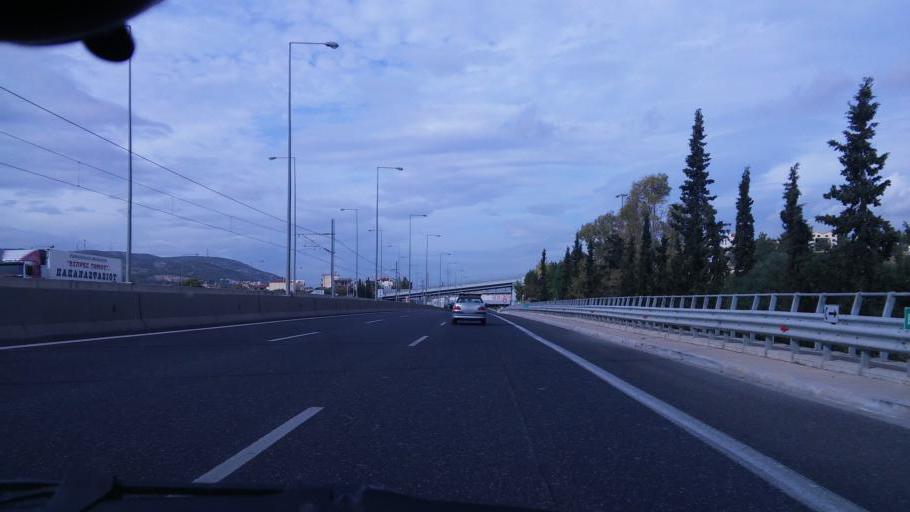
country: GR
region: Attica
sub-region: Nomarchia Dytikis Attikis
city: Zefyri
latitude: 38.0669
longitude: 23.7330
